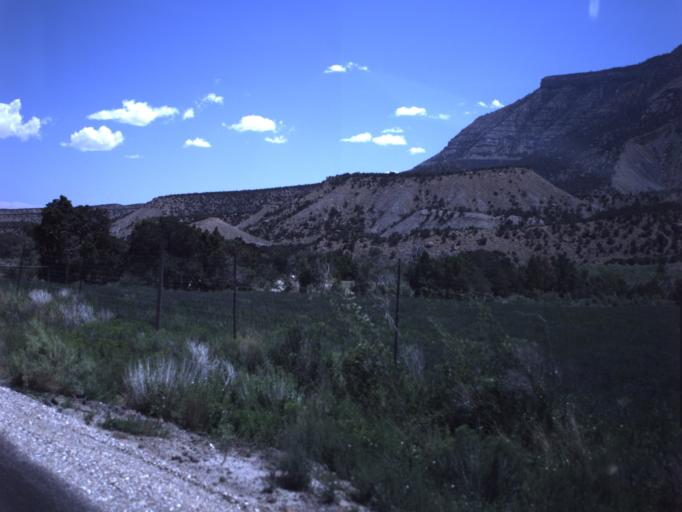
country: US
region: Utah
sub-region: Emery County
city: Orangeville
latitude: 39.2749
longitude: -111.1675
